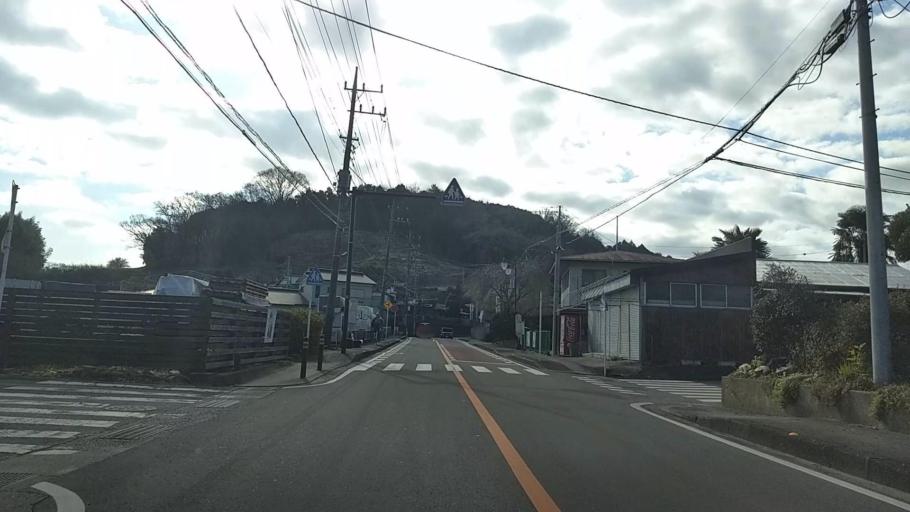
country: JP
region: Kanagawa
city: Isehara
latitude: 35.4395
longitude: 139.3017
